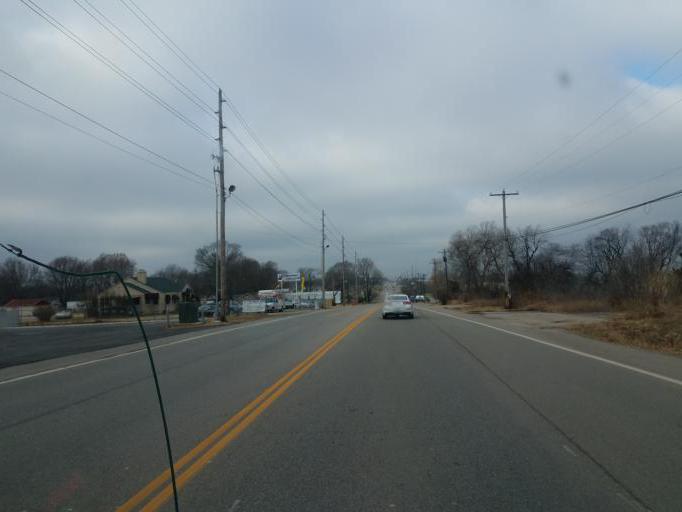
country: US
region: Missouri
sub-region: Greene County
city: Springfield
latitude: 37.2384
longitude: -93.2076
